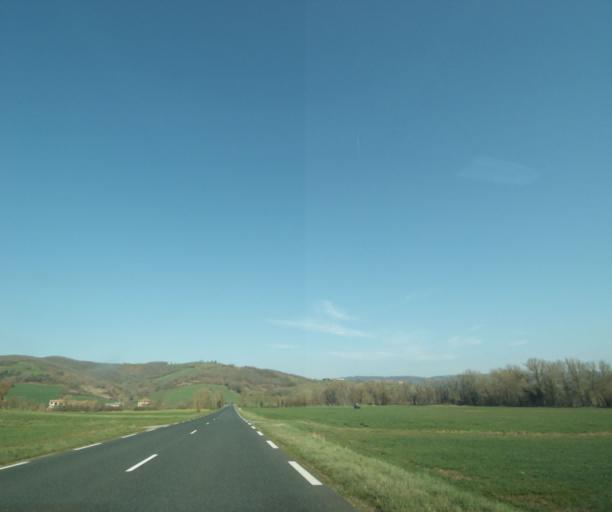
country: FR
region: Midi-Pyrenees
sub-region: Departement de l'Aveyron
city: Saint-Affrique
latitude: 43.9205
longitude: 2.8236
